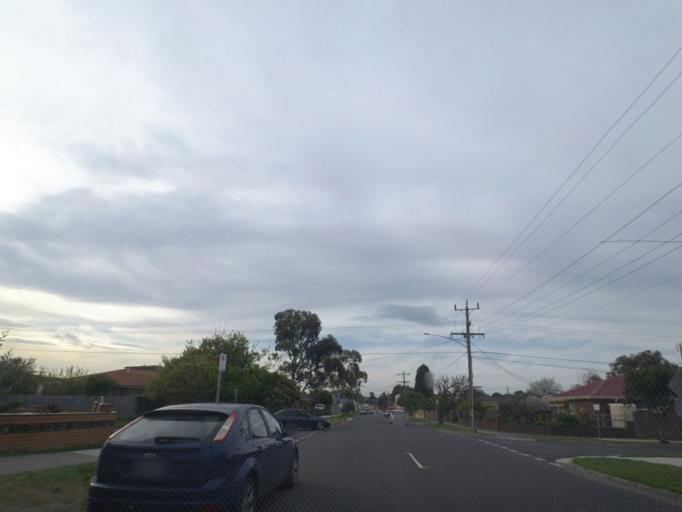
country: AU
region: Victoria
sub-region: Knox
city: Ferntree Gully
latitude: -37.8855
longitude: 145.2760
